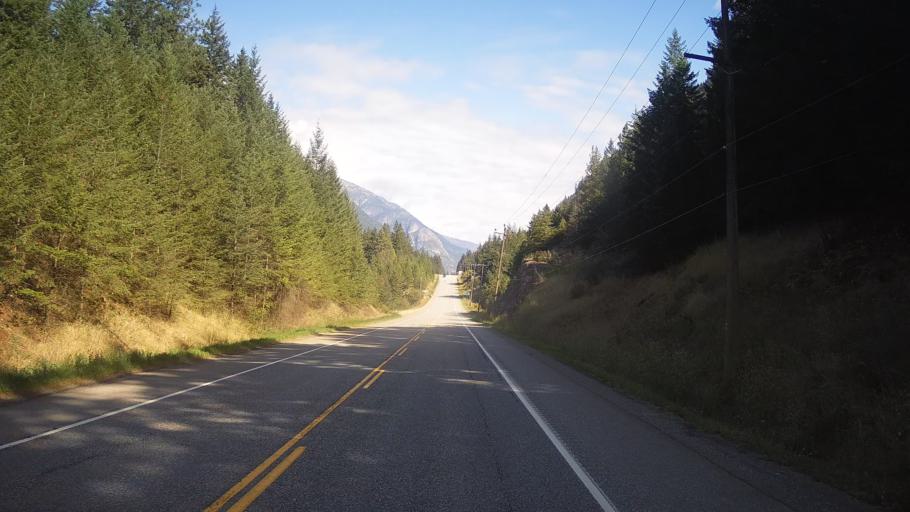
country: CA
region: British Columbia
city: Hope
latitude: 50.0293
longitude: -121.5292
